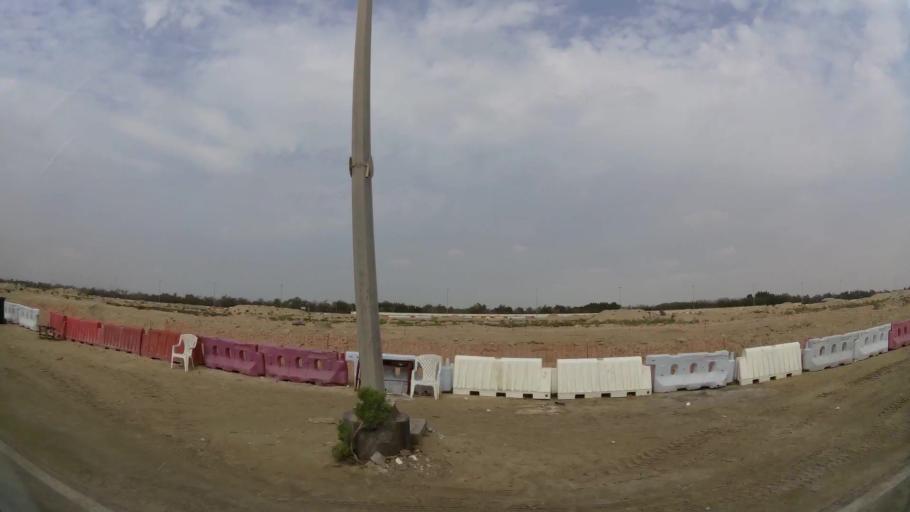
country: AE
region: Abu Dhabi
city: Abu Dhabi
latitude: 24.6474
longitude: 54.7275
